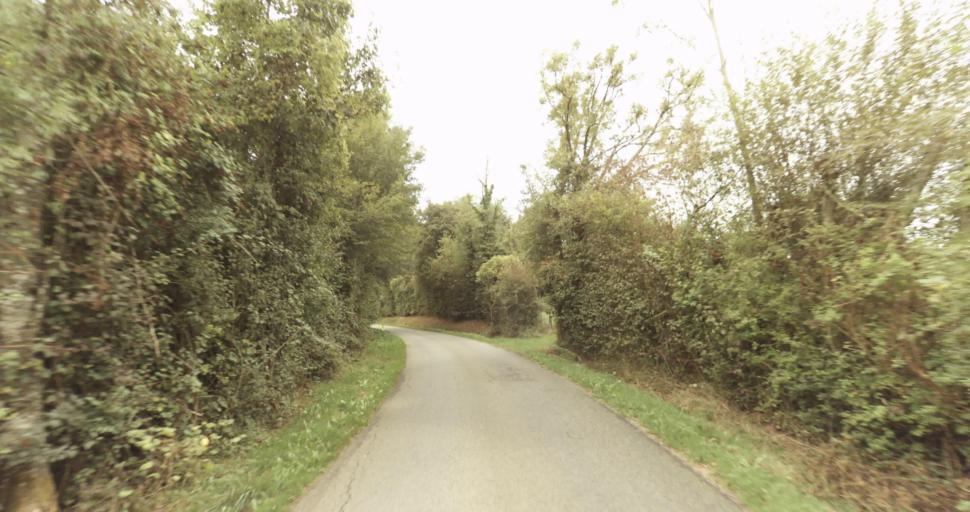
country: FR
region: Lower Normandy
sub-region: Departement de l'Orne
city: Gace
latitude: 48.7413
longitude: 0.3353
